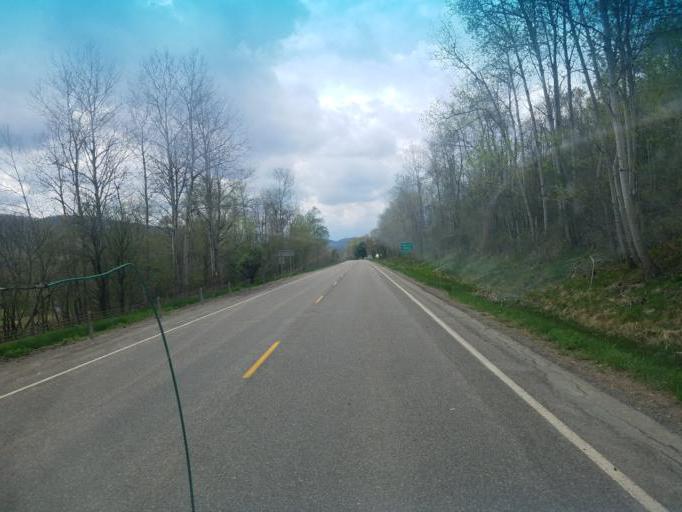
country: US
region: New York
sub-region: Allegany County
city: Andover
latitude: 42.0115
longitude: -77.8397
